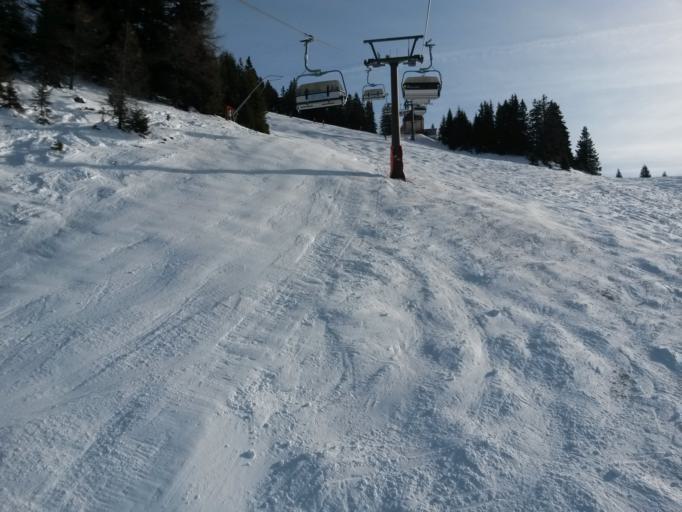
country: AT
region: Salzburg
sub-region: Politischer Bezirk Sankt Johann im Pongau
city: Dorfgastein
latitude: 47.2352
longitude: 13.1339
